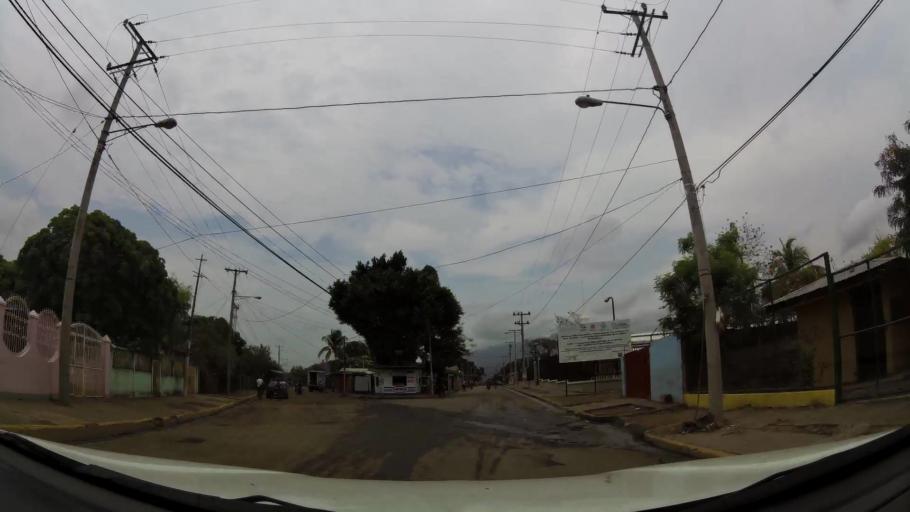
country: NI
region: Granada
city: Granada
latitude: 11.9204
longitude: -85.9551
